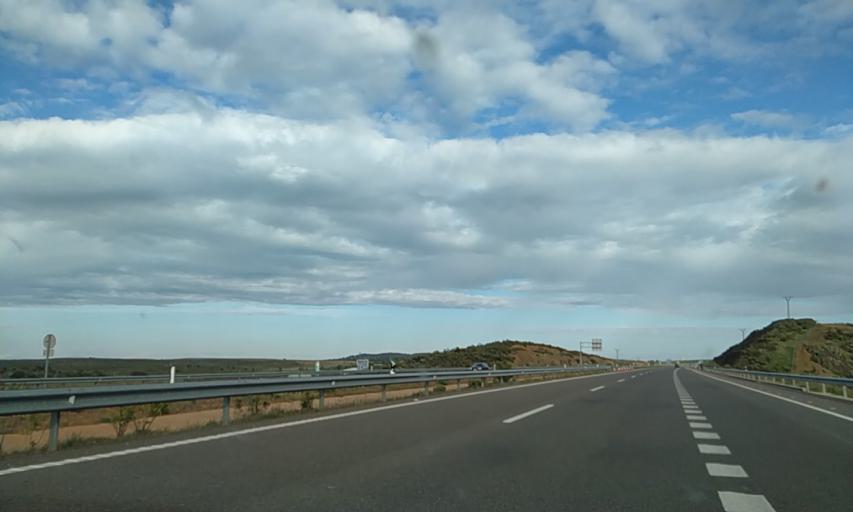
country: ES
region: Extremadura
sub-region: Provincia de Caceres
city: Casas de Don Gomez
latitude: 40.0259
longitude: -6.6059
